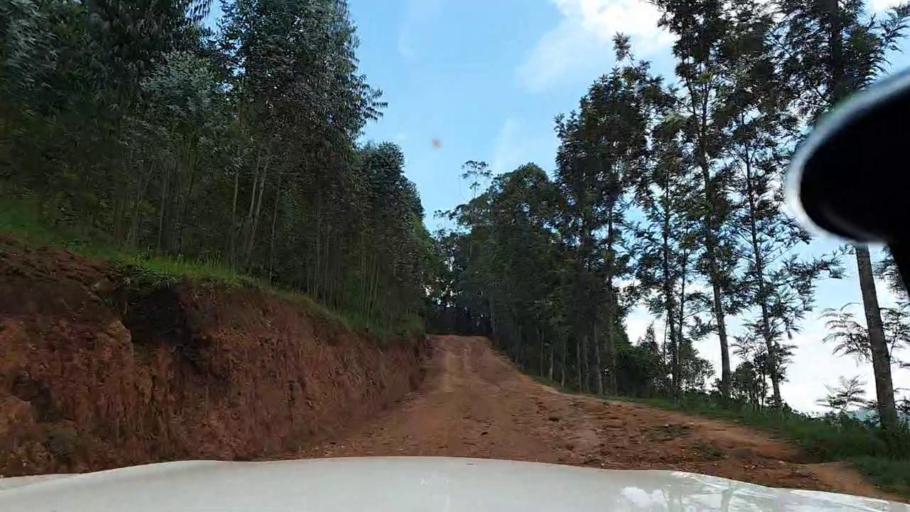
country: RW
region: Southern Province
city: Gitarama
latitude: -1.8062
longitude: 29.7988
